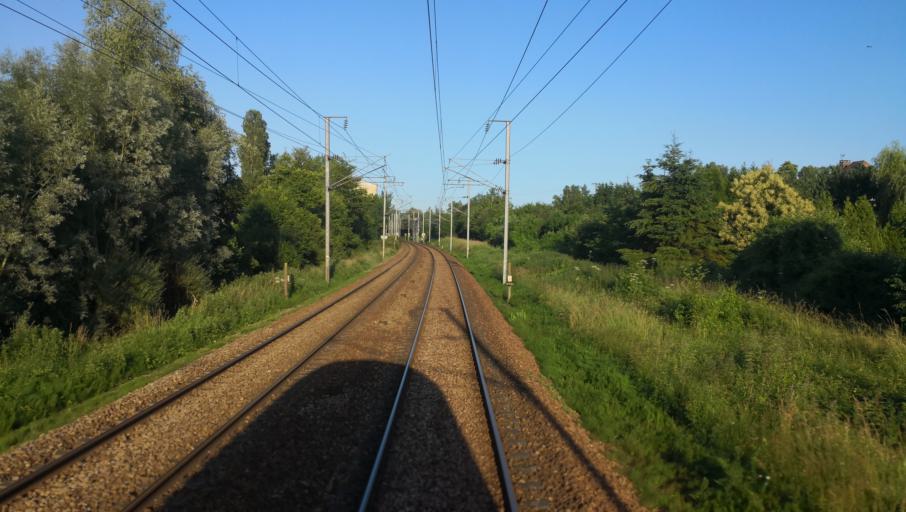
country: FR
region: Lower Normandy
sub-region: Departement du Calvados
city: Beuvillers
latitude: 49.1281
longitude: 0.2570
